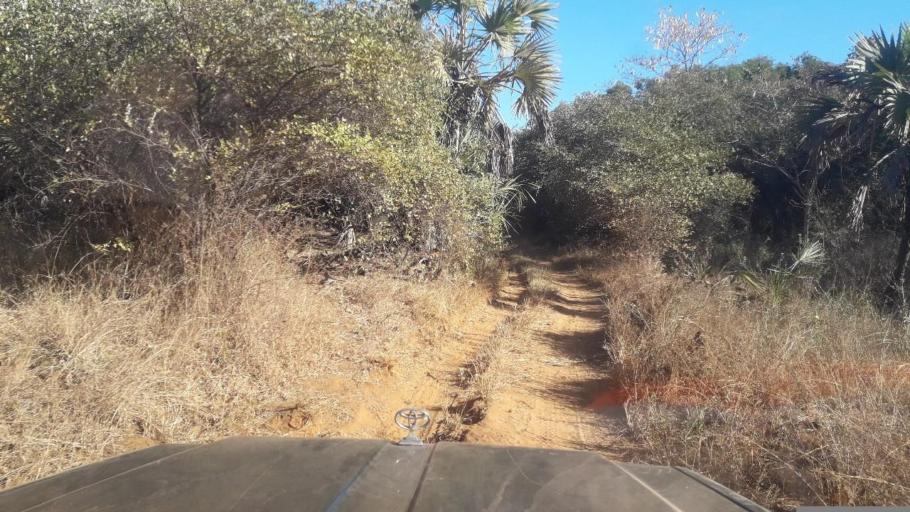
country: MG
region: Boeny
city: Sitampiky
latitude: -16.4028
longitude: 45.5980
